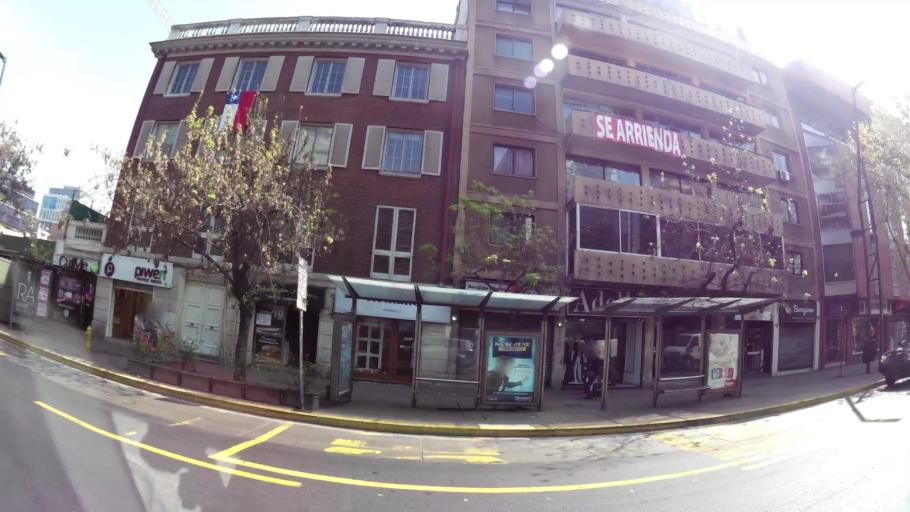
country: CL
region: Santiago Metropolitan
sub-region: Provincia de Santiago
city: Villa Presidente Frei, Nunoa, Santiago, Chile
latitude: -33.4205
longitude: -70.6077
